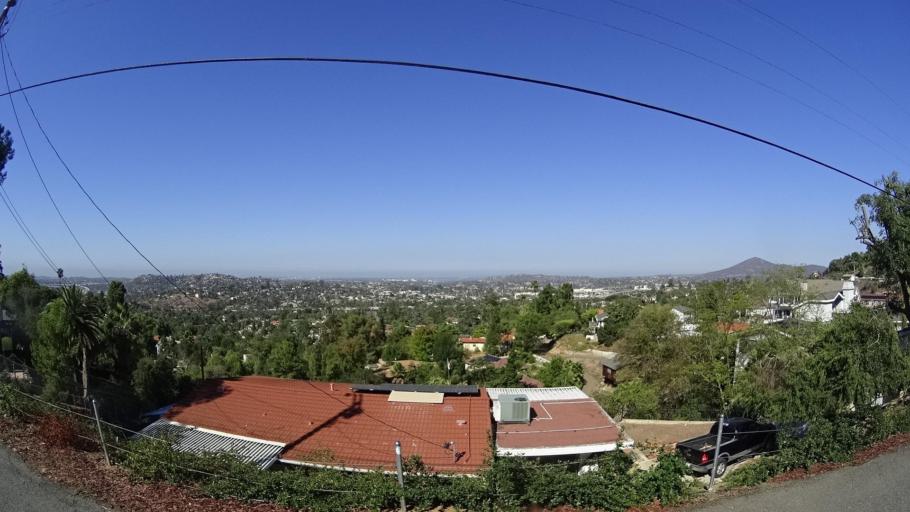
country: US
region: California
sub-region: San Diego County
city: Casa de Oro-Mount Helix
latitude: 32.7681
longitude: -116.9892
